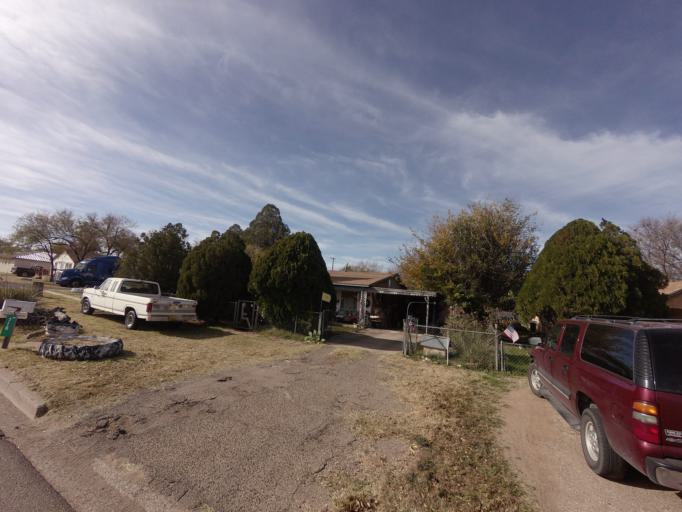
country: US
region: New Mexico
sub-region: Curry County
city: Clovis
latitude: 34.4055
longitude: -103.1940
